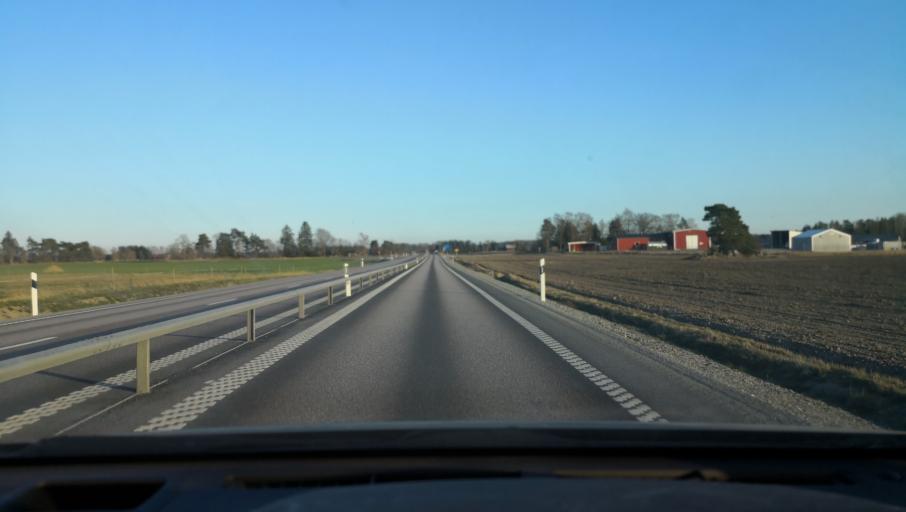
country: SE
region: Uppsala
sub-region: Enkopings Kommun
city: Enkoping
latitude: 59.6889
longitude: 17.0333
